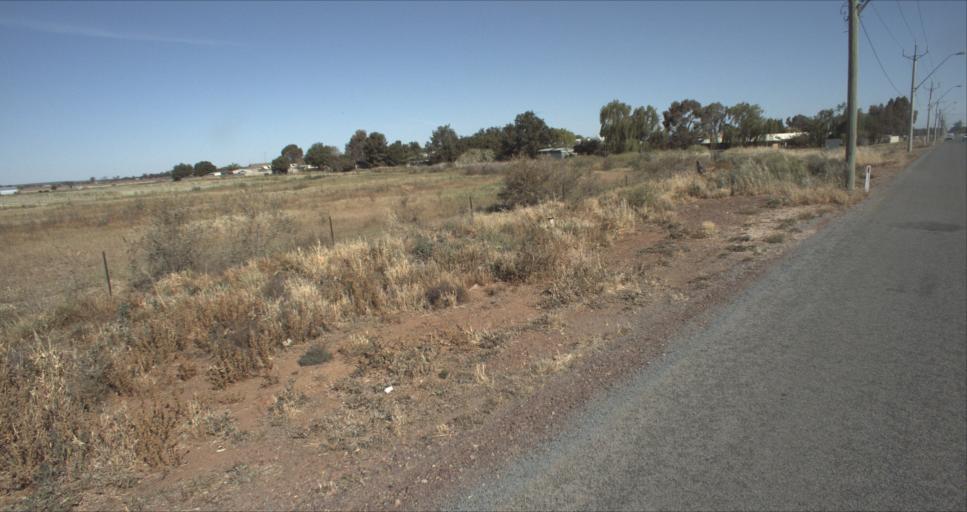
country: AU
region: New South Wales
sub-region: Leeton
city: Leeton
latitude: -34.5449
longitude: 146.4183
